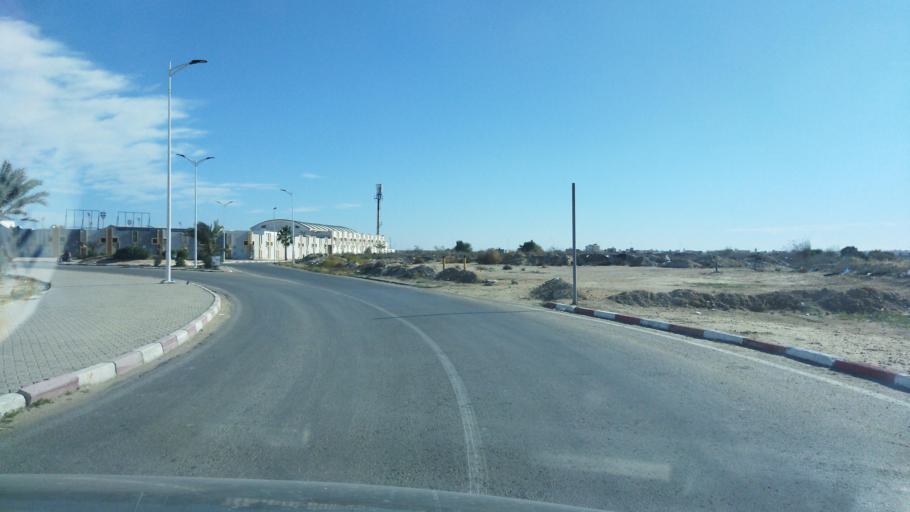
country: TN
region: Qabis
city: Gabes
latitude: 33.8875
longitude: 10.1163
